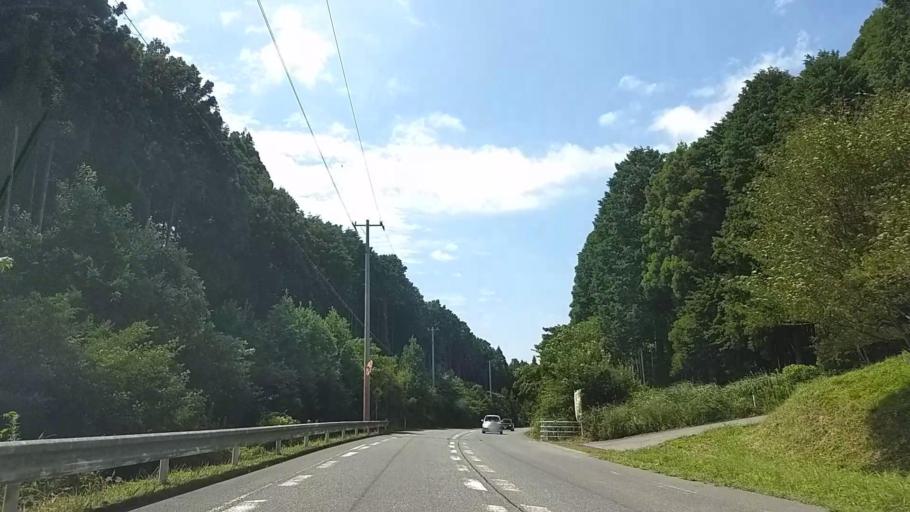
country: JP
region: Shizuoka
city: Fuji
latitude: 35.2447
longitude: 138.7227
